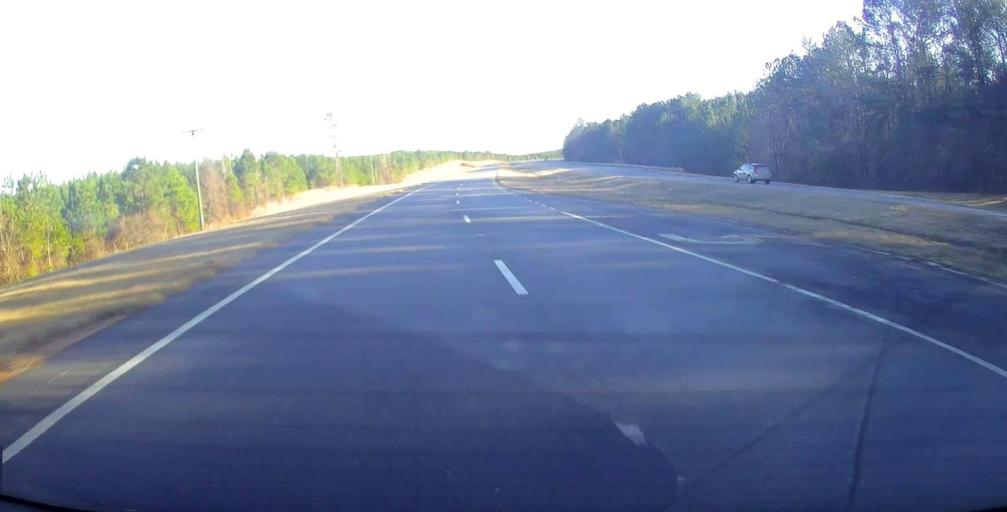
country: US
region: Georgia
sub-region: Upson County
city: Thomaston
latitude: 32.7840
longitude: -84.2464
